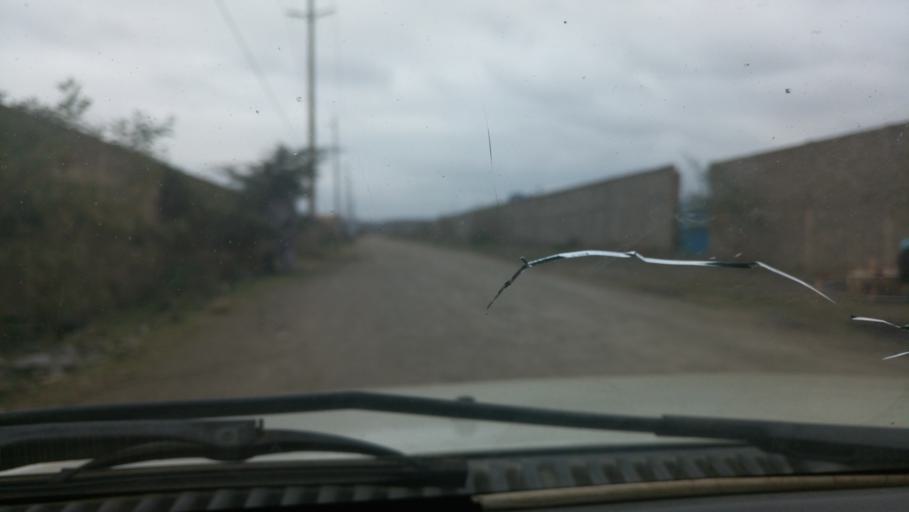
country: KE
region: Nairobi Area
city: Pumwani
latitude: -1.3372
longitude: 36.8869
